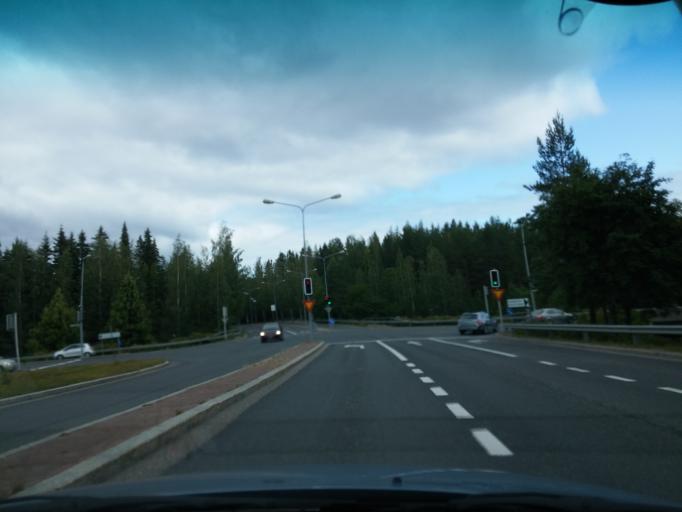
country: FI
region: Northern Savo
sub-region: Kuopio
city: Kuopio
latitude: 62.8376
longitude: 27.6543
